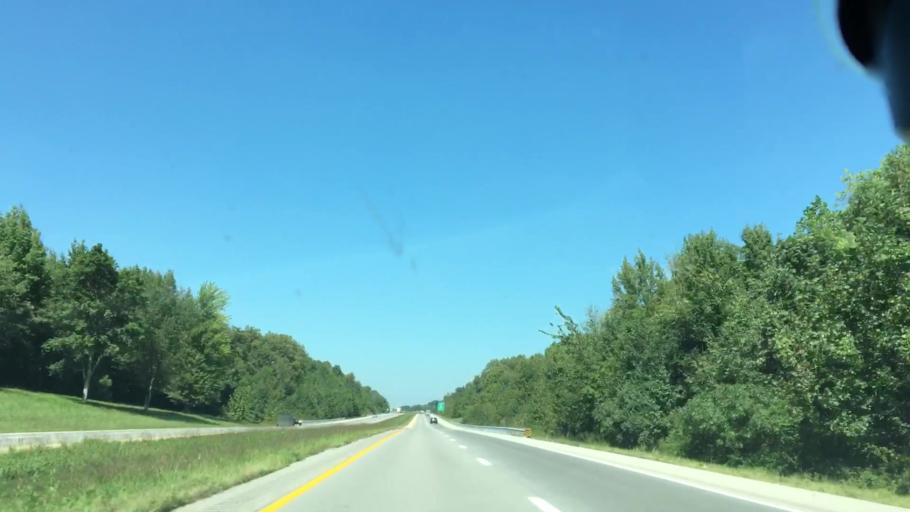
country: US
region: Kentucky
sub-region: Webster County
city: Sebree
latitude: 37.6758
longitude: -87.5134
